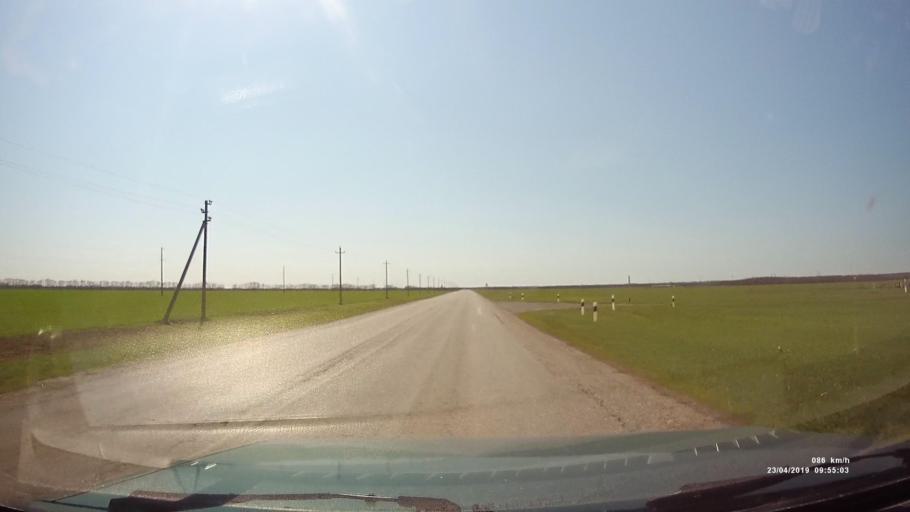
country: RU
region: Rostov
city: Orlovskiy
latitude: 46.8137
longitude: 42.0598
